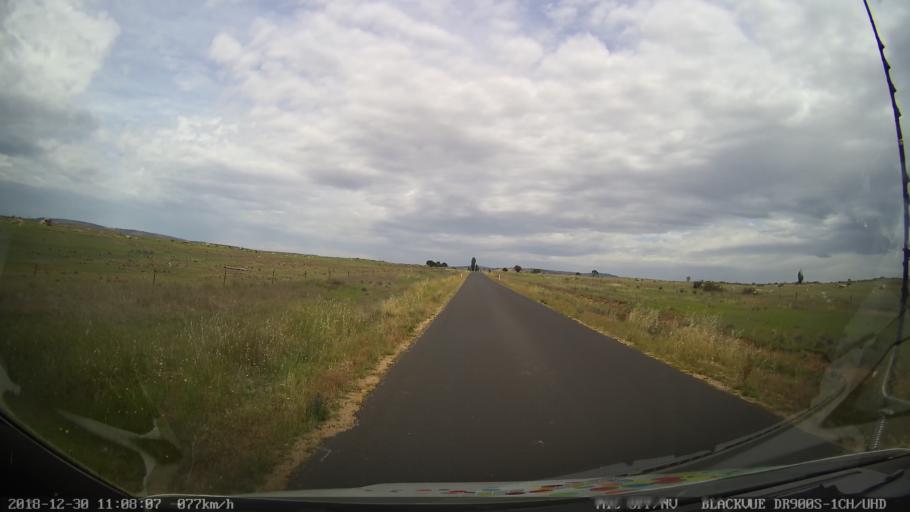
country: AU
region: New South Wales
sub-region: Snowy River
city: Berridale
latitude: -36.5022
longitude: 148.8110
